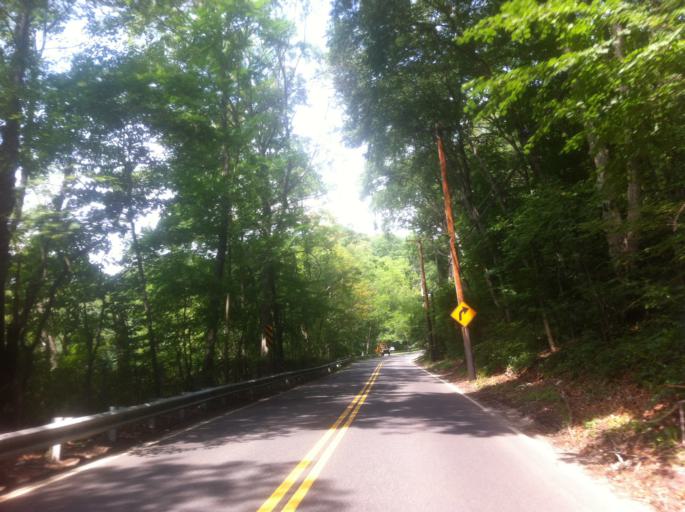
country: US
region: New York
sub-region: Nassau County
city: Upper Brookville
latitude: 40.8673
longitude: -73.5683
